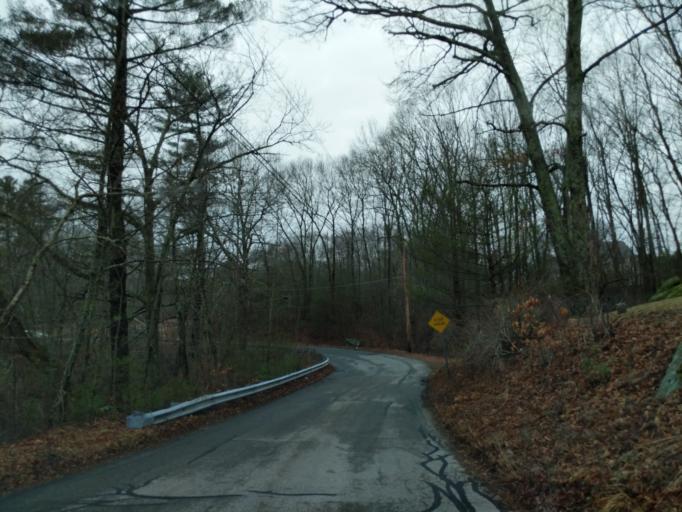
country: US
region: Massachusetts
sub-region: Worcester County
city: Whitinsville
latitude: 42.1040
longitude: -71.6893
